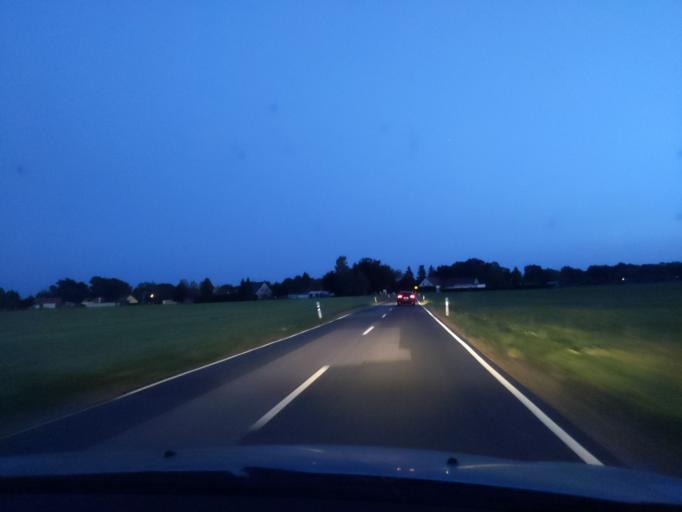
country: DE
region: Saxony
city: Malschwitz
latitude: 51.2695
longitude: 14.5227
